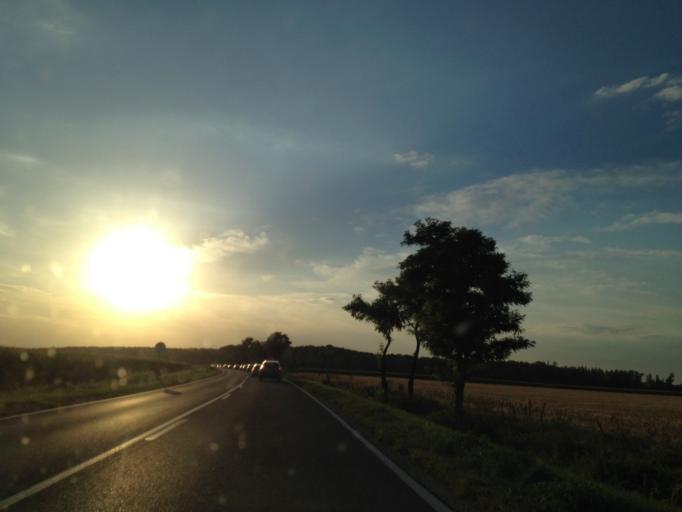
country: HU
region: Gyor-Moson-Sopron
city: Kimle
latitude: 47.8249
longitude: 17.3257
